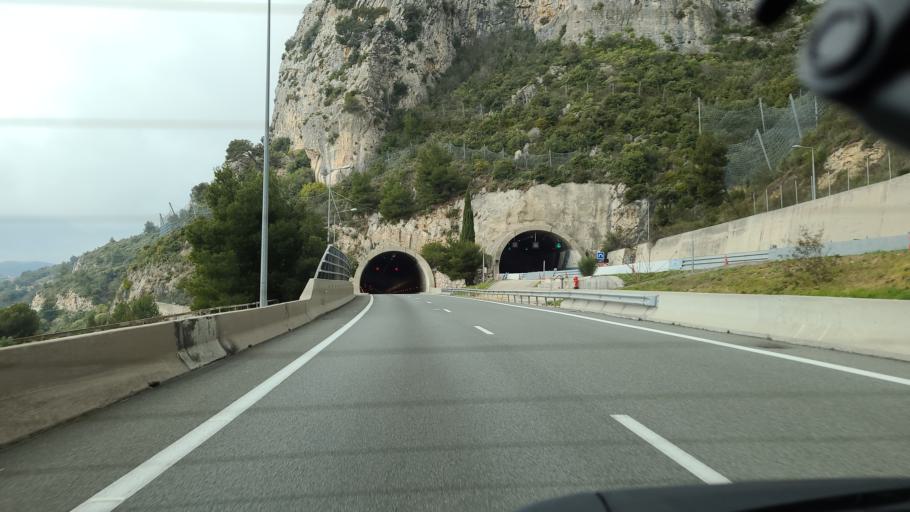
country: MC
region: Commune de Monaco
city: Saint-Roman
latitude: 43.7588
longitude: 7.4384
